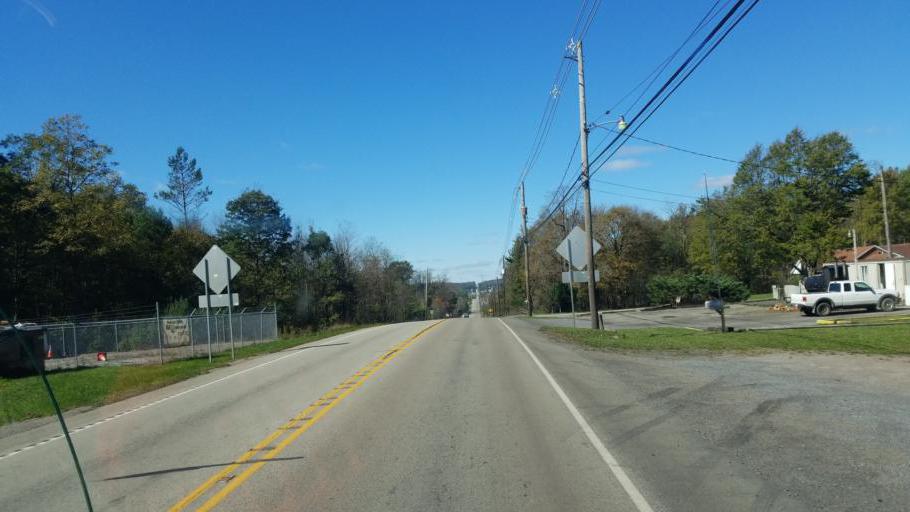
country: US
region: Pennsylvania
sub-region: Somerset County
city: Central City
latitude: 40.0595
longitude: -78.8310
